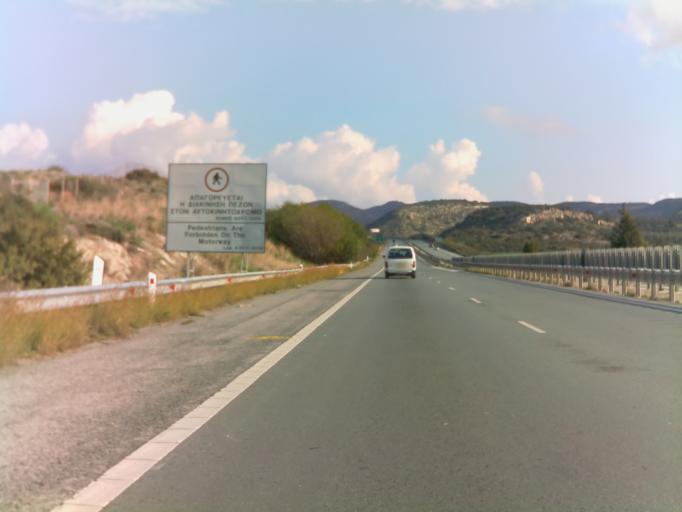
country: CY
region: Larnaka
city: Kofinou
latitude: 34.7627
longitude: 33.3281
